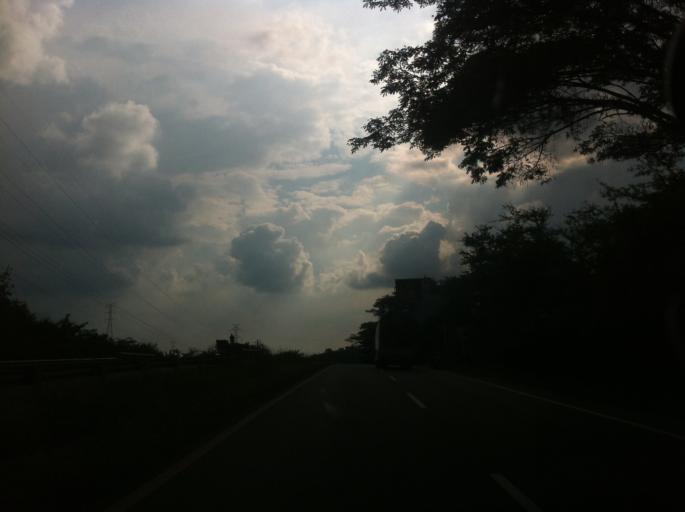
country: CO
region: Valle del Cauca
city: Tulua
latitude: 4.0671
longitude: -76.1799
